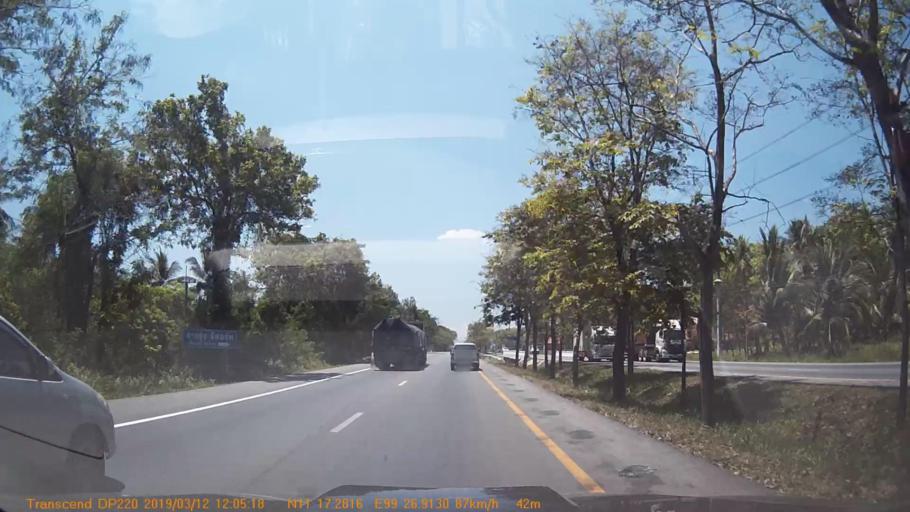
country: TH
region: Prachuap Khiri Khan
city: Bang Saphan
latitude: 11.2879
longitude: 99.4484
